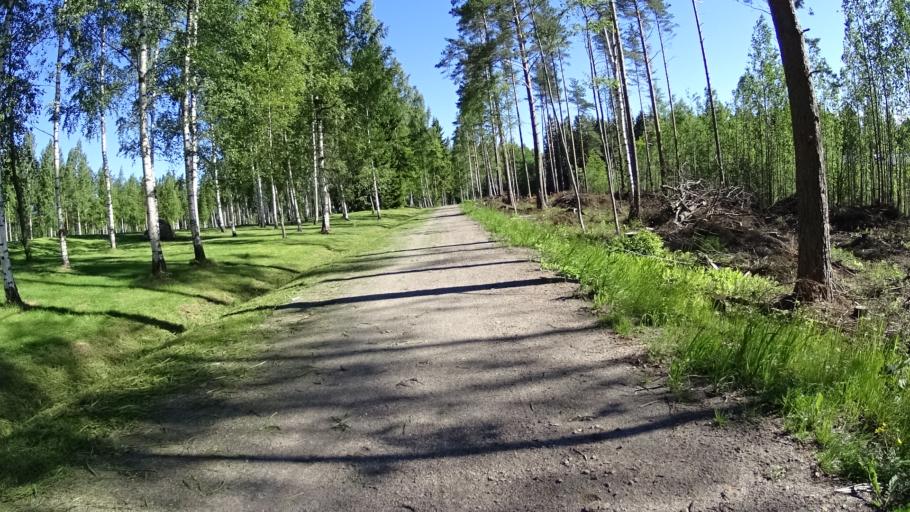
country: FI
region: Uusimaa
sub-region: Helsinki
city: Kilo
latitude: 60.3229
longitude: 24.8175
